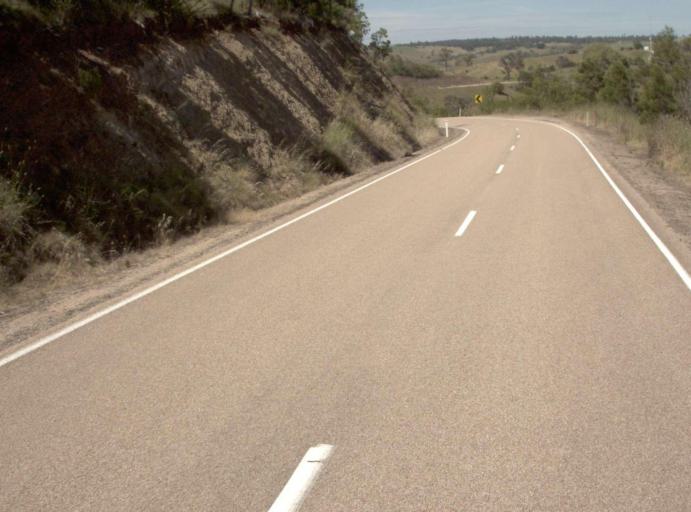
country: AU
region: Victoria
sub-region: East Gippsland
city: Lakes Entrance
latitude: -37.4868
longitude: 148.1872
